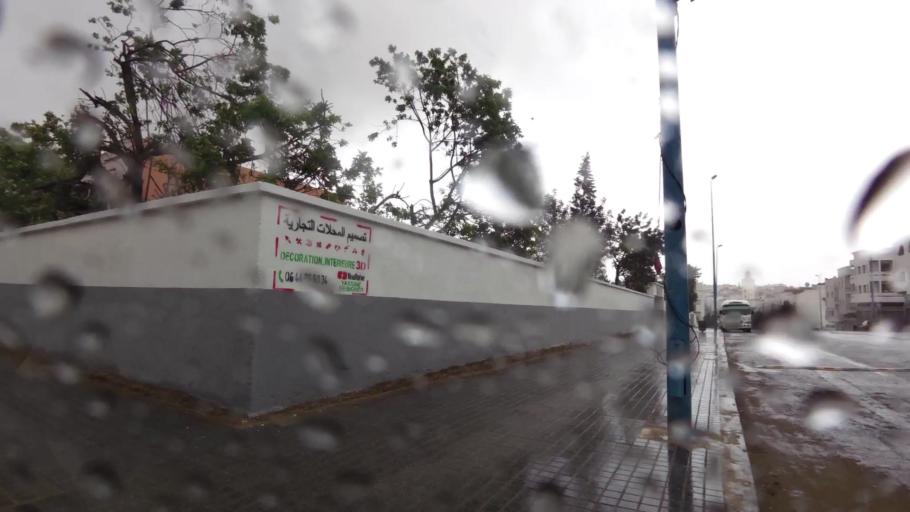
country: MA
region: Grand Casablanca
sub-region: Casablanca
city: Casablanca
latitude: 33.5465
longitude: -7.6802
